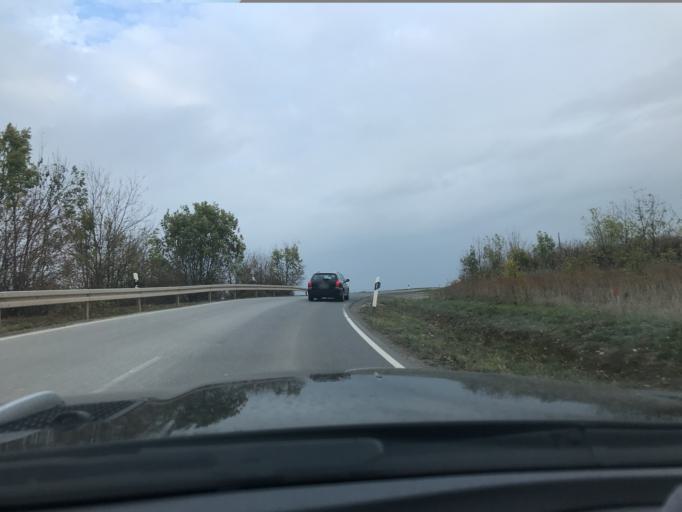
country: DE
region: Hesse
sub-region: Regierungsbezirk Kassel
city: Calden
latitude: 51.4255
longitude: 9.3711
